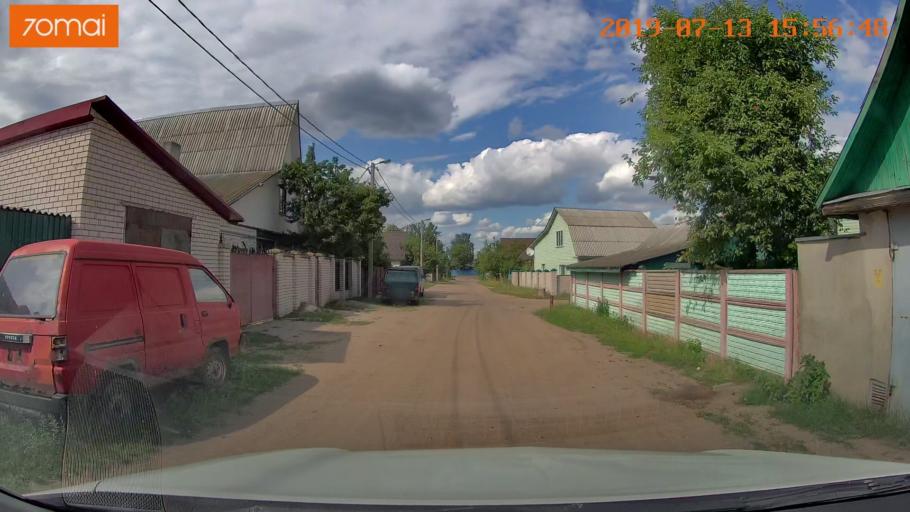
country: BY
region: Mogilev
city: Babruysk
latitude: 53.1451
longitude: 29.2024
